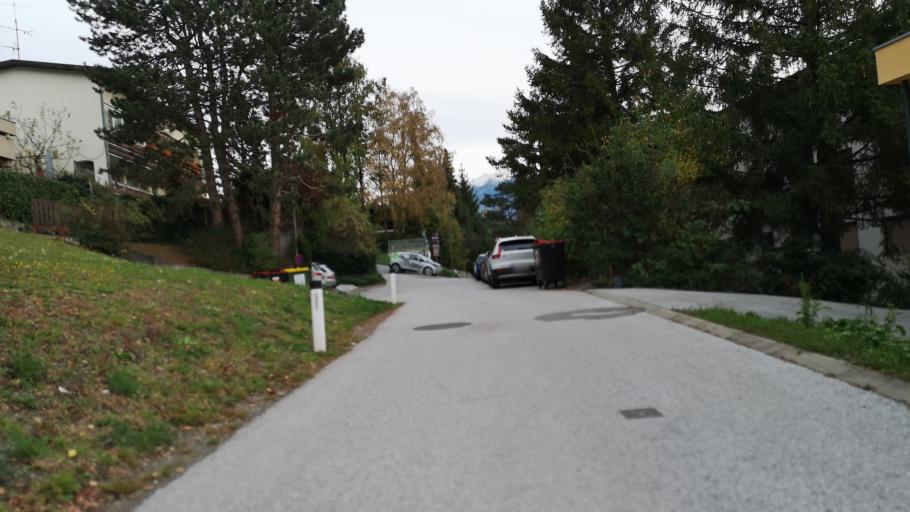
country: AT
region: Tyrol
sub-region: Politischer Bezirk Innsbruck Land
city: Vols
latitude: 47.2668
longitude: 11.3616
